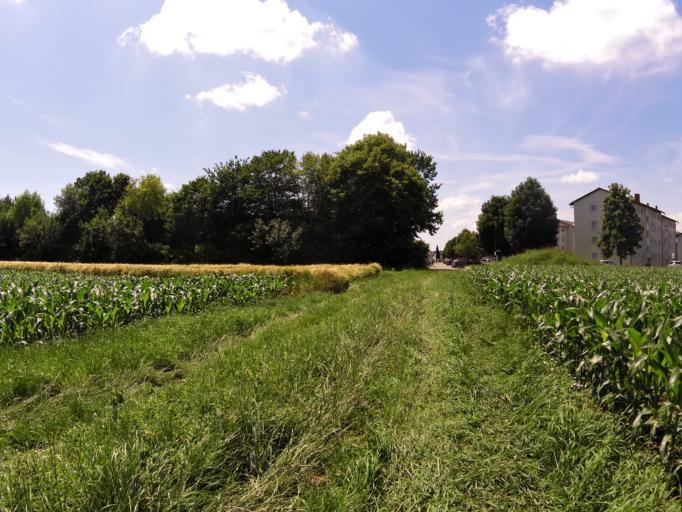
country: DE
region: Baden-Wuerttemberg
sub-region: Freiburg Region
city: Kippenheim
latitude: 48.3218
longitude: 7.8084
